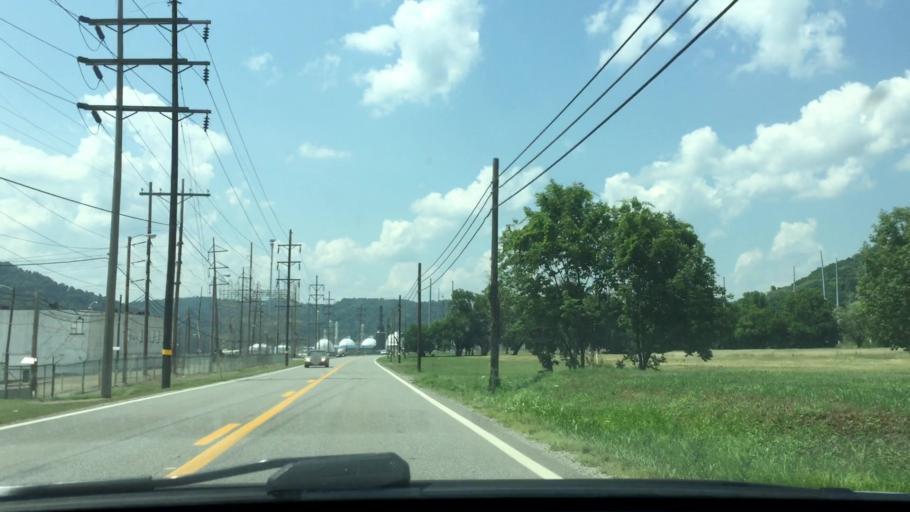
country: US
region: West Virginia
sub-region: Wetzel County
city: New Martinsville
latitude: 39.7515
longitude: -80.8533
